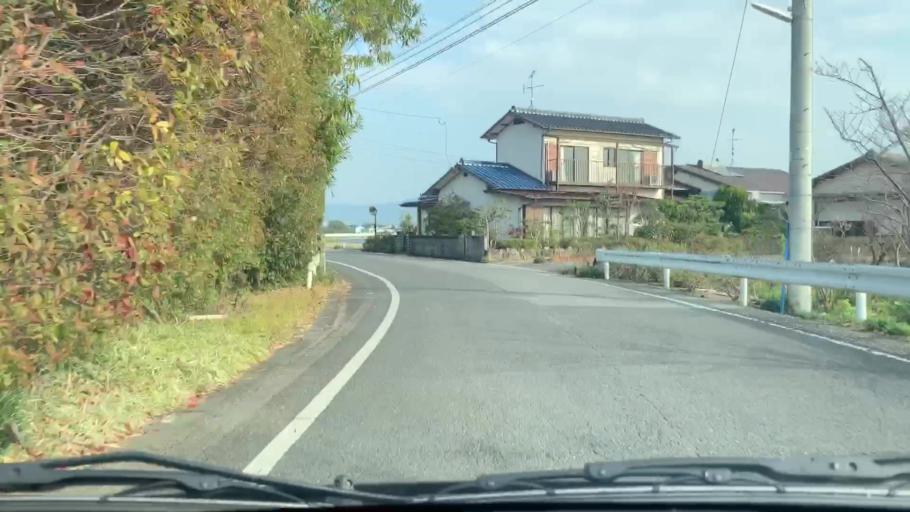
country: JP
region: Saga Prefecture
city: Saga-shi
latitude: 33.2484
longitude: 130.2581
